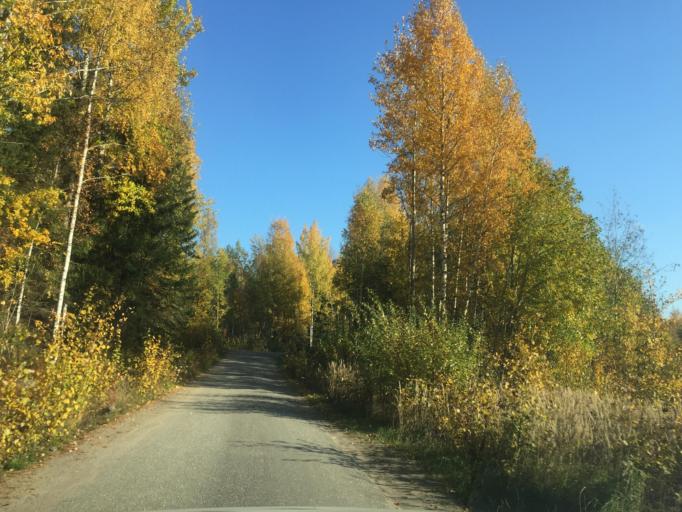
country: RU
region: Leningrad
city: Priozersk
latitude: 61.2895
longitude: 30.0824
